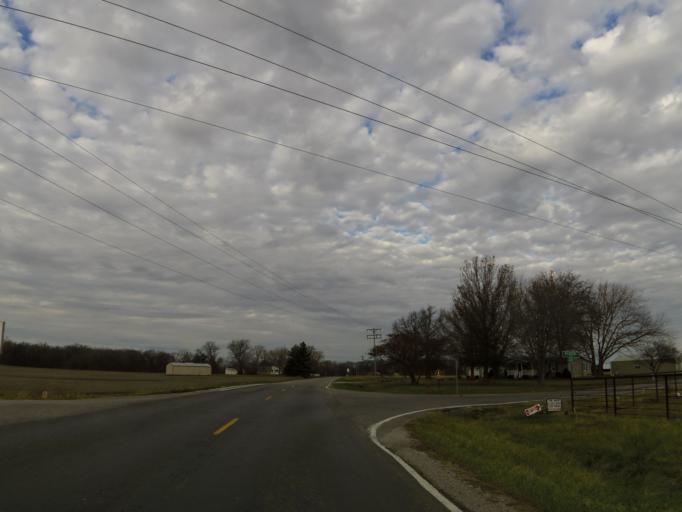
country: US
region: Illinois
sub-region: Jefferson County
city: Mount Vernon
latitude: 38.3730
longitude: -89.0064
